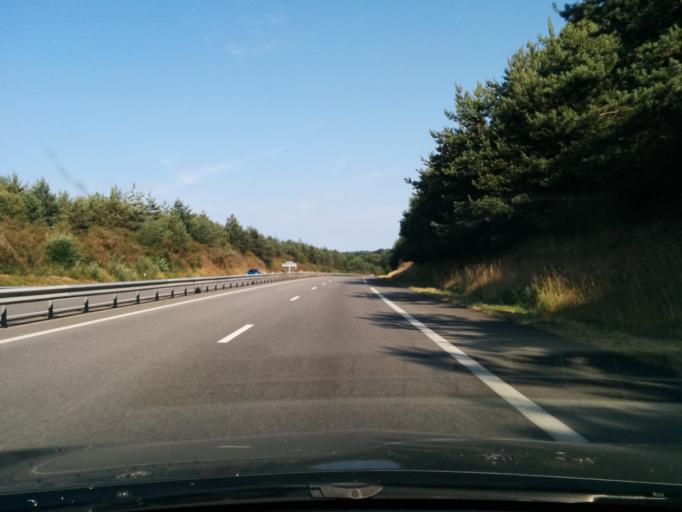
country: FR
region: Limousin
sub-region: Departement de la Haute-Vienne
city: Saint-Germain-les-Belles
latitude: 45.5913
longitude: 1.4609
